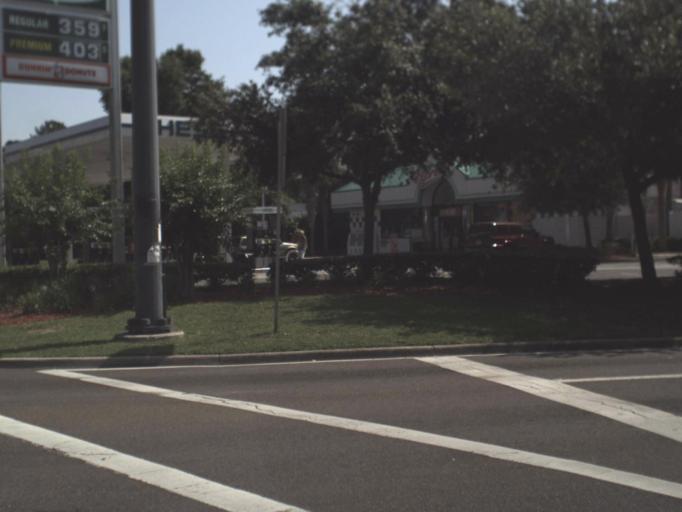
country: US
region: Florida
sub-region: Clay County
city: Bellair-Meadowbrook Terrace
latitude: 30.2847
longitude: -81.7552
